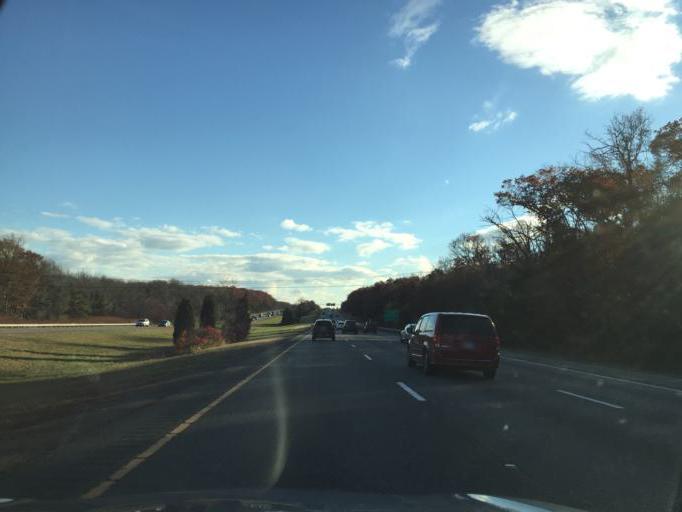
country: US
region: Massachusetts
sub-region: Bristol County
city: Attleboro
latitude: 41.9803
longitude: -71.2944
